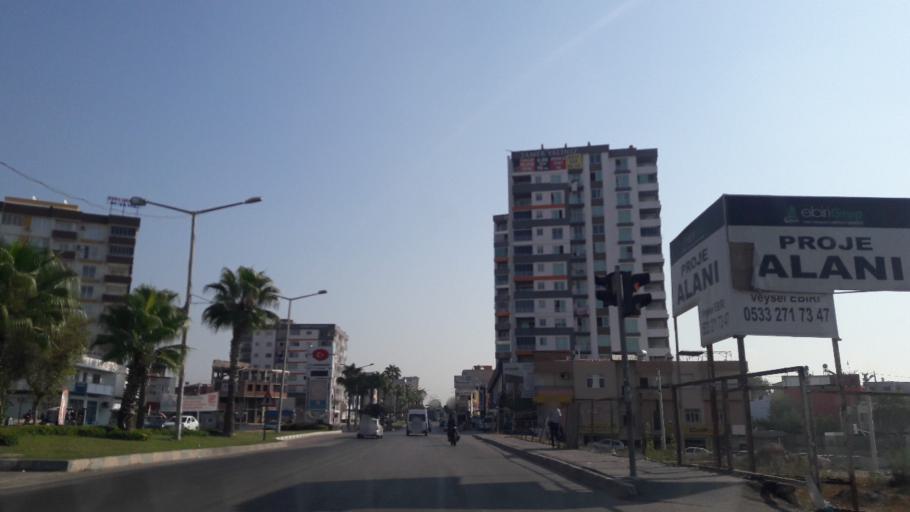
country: TR
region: Adana
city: Yuregir
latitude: 37.0298
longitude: 35.4060
